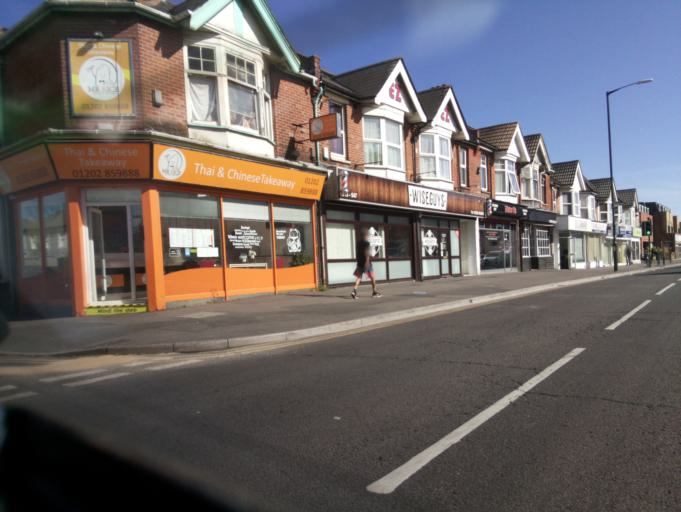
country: GB
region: England
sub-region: Bournemouth
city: Bournemouth
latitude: 50.7461
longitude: -1.8781
